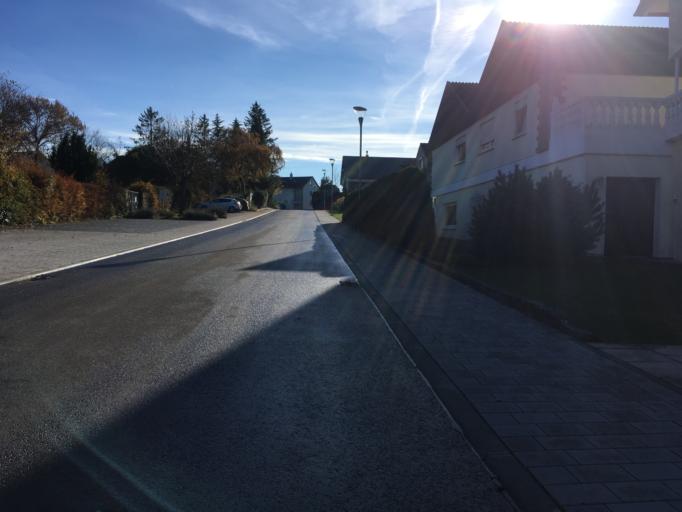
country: DE
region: Baden-Wuerttemberg
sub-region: Regierungsbezirk Stuttgart
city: Gemmingen
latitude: 49.1451
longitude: 8.9617
